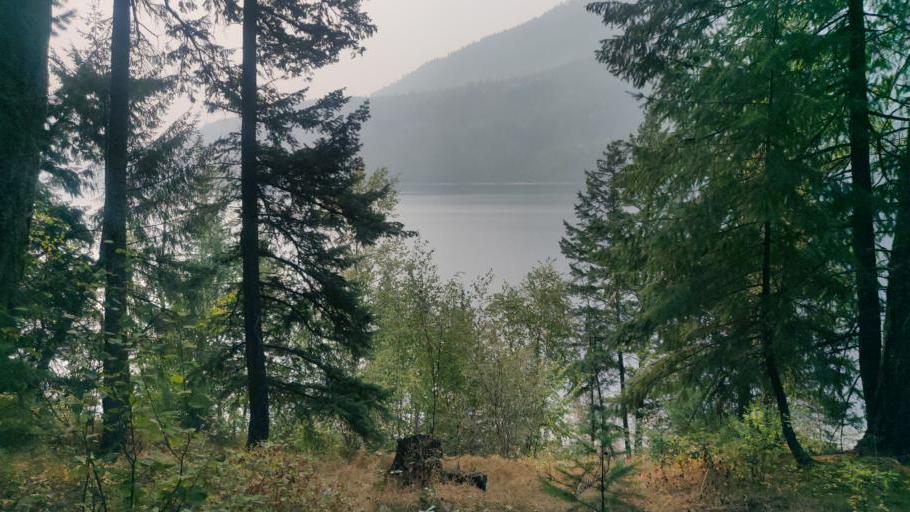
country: CA
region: British Columbia
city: Chase
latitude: 51.0763
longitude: -119.7637
